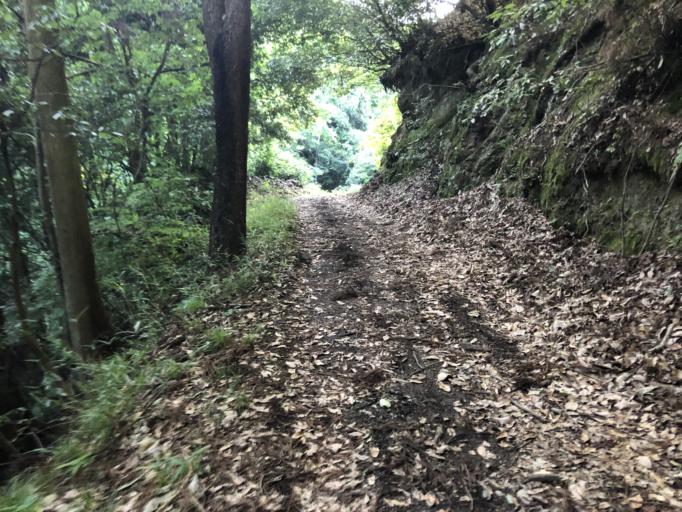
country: JP
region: Kyoto
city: Kameoka
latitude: 34.9891
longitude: 135.6223
